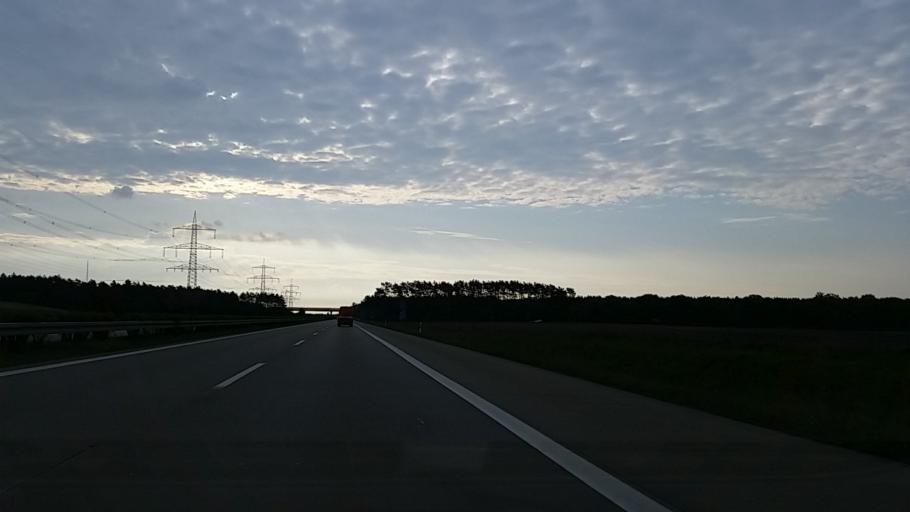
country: DE
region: Mecklenburg-Vorpommern
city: Zarrentin
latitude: 53.5113
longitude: 10.8871
